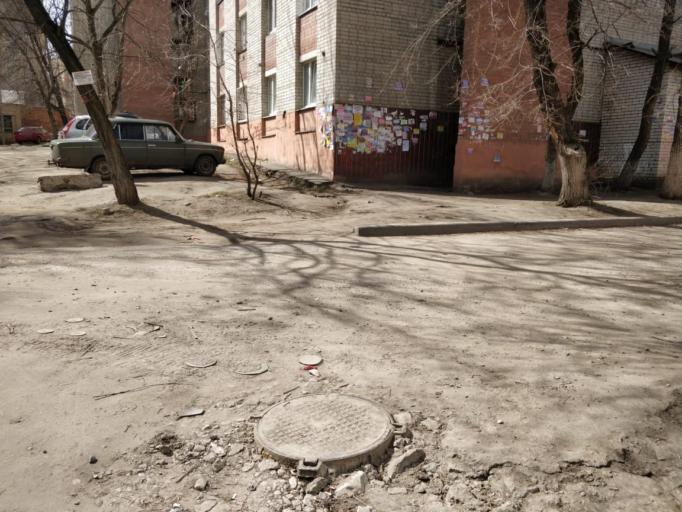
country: RU
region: Voronezj
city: Pridonskoy
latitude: 51.6835
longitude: 39.1241
